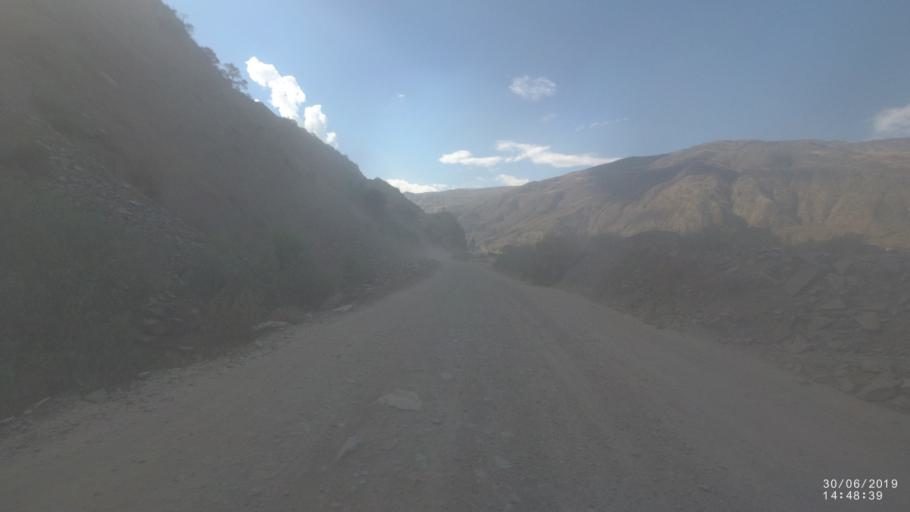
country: BO
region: Cochabamba
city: Irpa Irpa
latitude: -17.7880
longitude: -66.3425
